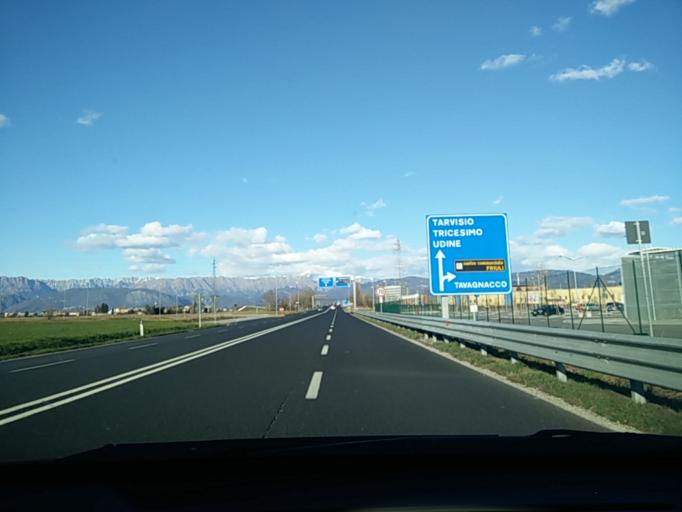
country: IT
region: Friuli Venezia Giulia
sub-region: Provincia di Udine
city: Tavagnacco
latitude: 46.1165
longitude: 13.2194
